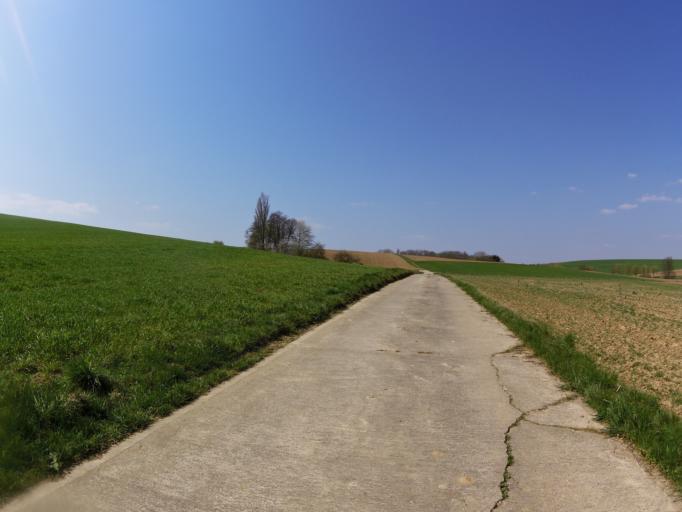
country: DE
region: Bavaria
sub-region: Regierungsbezirk Unterfranken
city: Dettelbach
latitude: 49.8185
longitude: 10.1469
